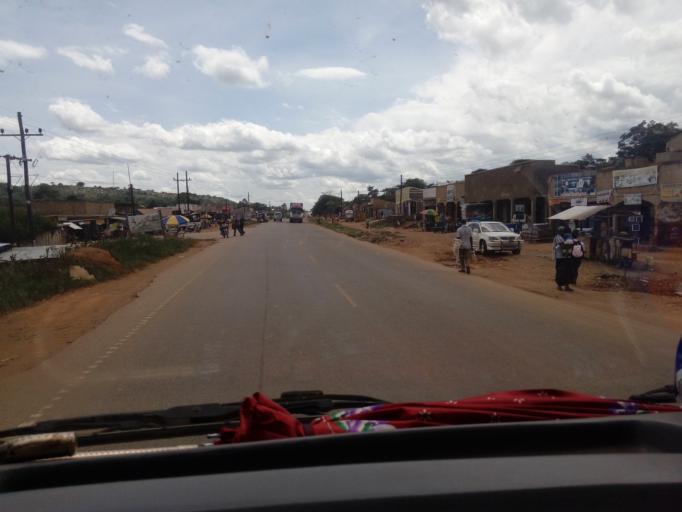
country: UG
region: Central Region
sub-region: Mubende District
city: Mubende
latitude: 0.4478
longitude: 31.6879
